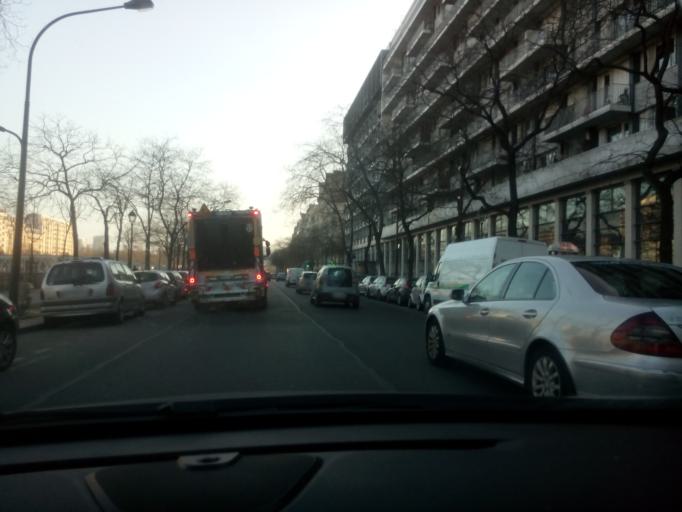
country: FR
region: Ile-de-France
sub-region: Paris
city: Paris
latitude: 48.8506
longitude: 2.3671
